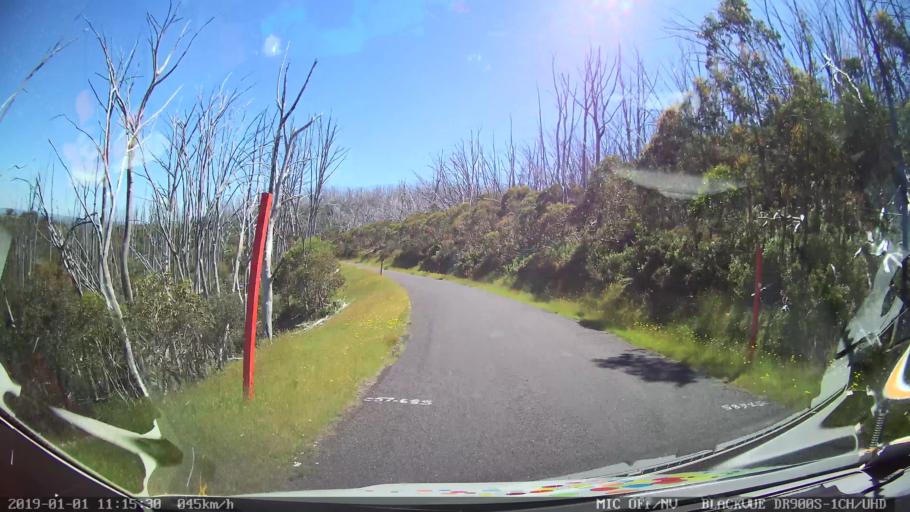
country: AU
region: New South Wales
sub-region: Snowy River
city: Jindabyne
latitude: -35.9447
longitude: 148.3872
